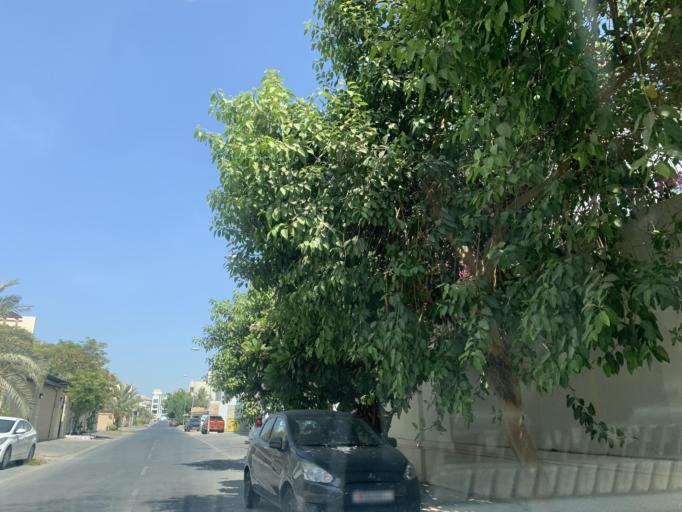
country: BH
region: Northern
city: Madinat `Isa
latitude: 26.1809
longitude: 50.4775
